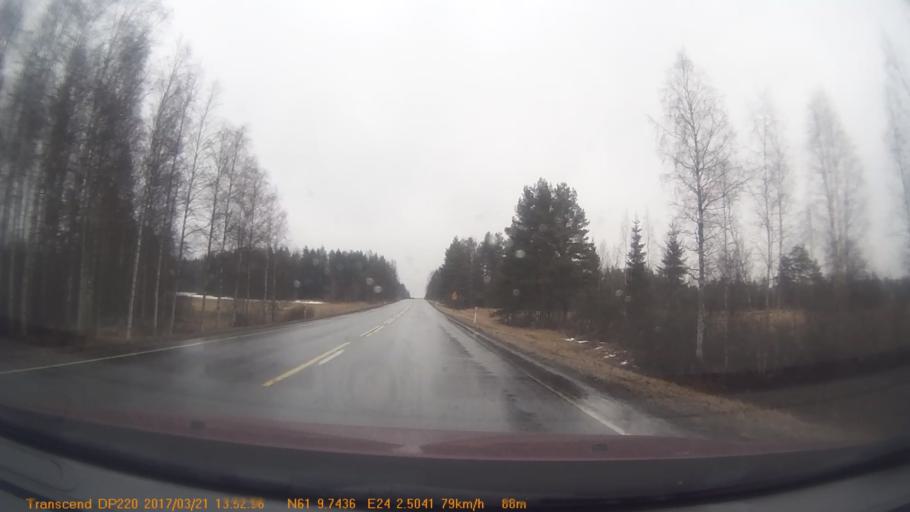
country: FI
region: Haeme
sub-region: Haemeenlinna
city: Kalvola
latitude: 61.1627
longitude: 24.0413
